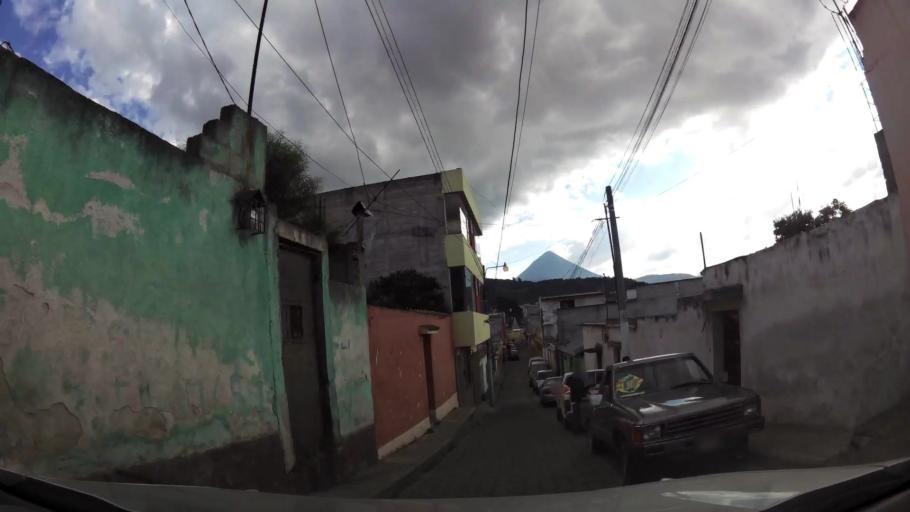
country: GT
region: Quetzaltenango
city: Quetzaltenango
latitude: 14.8389
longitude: -91.5269
